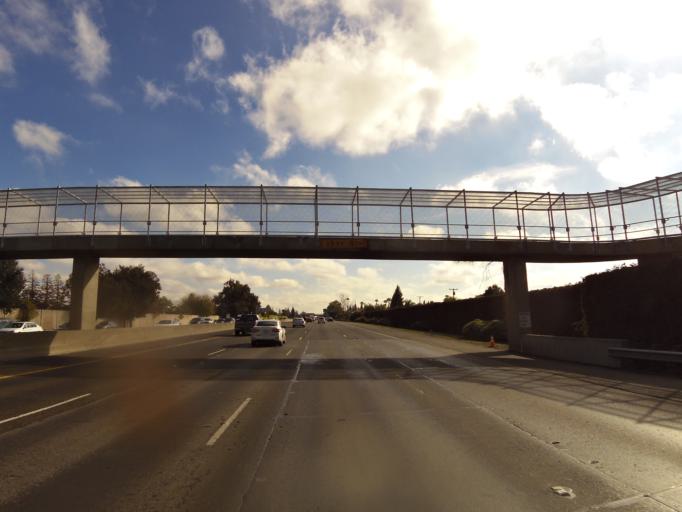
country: US
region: California
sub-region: Sacramento County
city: Parkway
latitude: 38.5026
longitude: -121.4531
